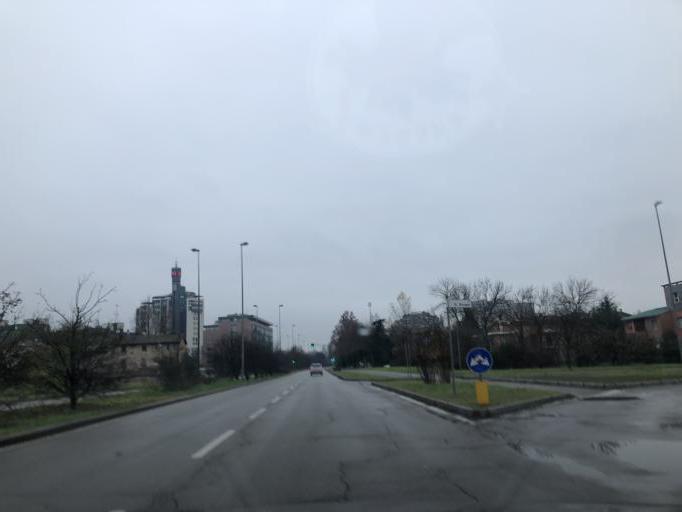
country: IT
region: Emilia-Romagna
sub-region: Provincia di Modena
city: Modena
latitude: 44.6394
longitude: 10.9006
